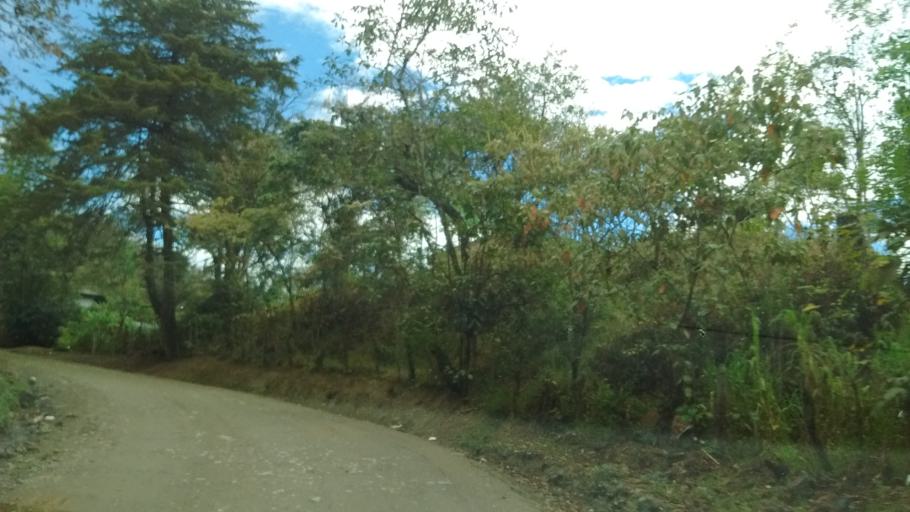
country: CO
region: Cauca
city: Almaguer
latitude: 1.8461
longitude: -76.9235
